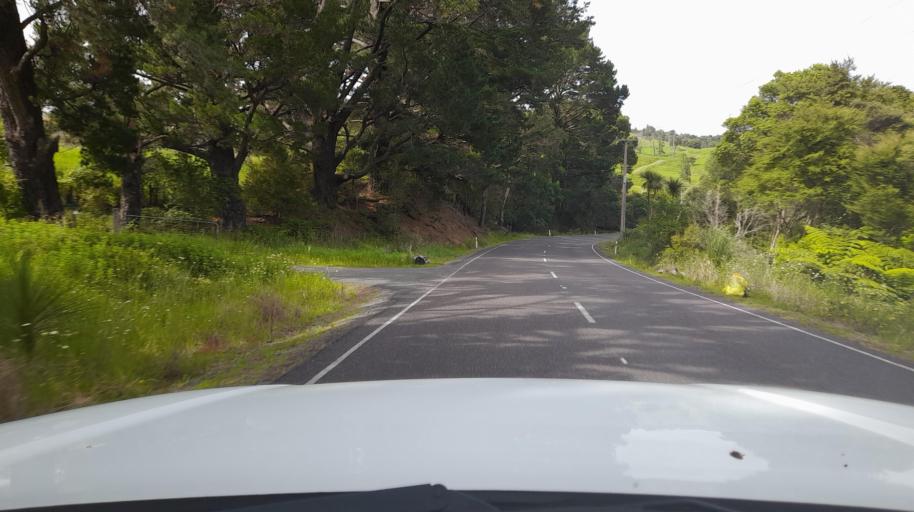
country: NZ
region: Northland
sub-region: Far North District
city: Taipa
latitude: -35.2391
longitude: 173.5419
